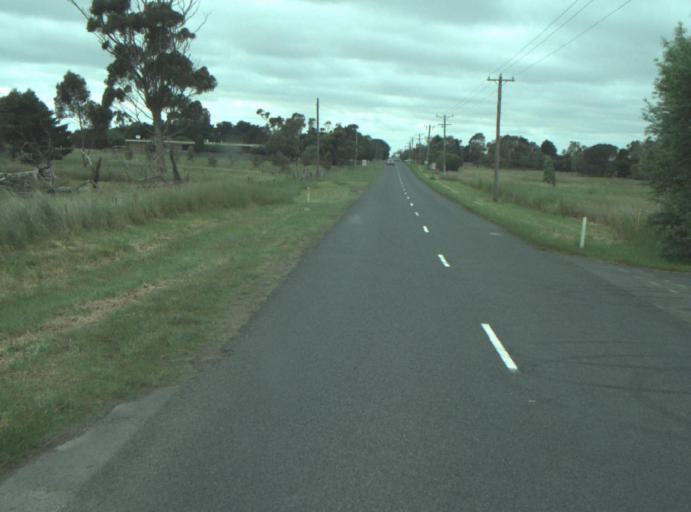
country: AU
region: Victoria
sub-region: Greater Geelong
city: Bell Post Hill
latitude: -38.0492
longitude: 144.3136
